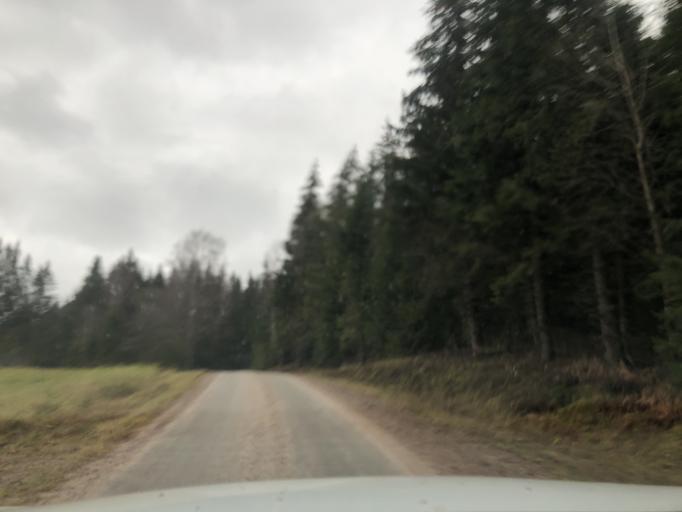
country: SE
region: Vaestra Goetaland
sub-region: Ulricehamns Kommun
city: Ulricehamn
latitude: 57.8689
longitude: 13.5565
